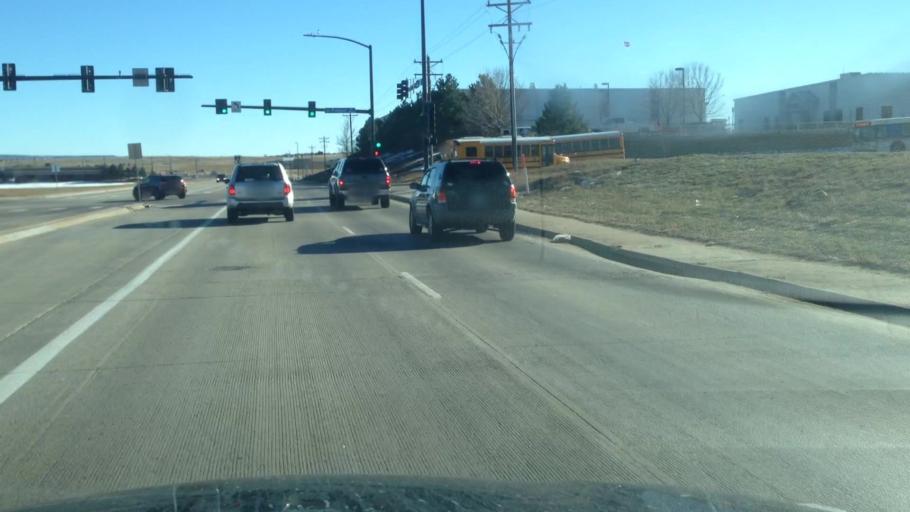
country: US
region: Colorado
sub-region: Arapahoe County
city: Dove Valley
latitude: 39.5869
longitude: -104.8164
